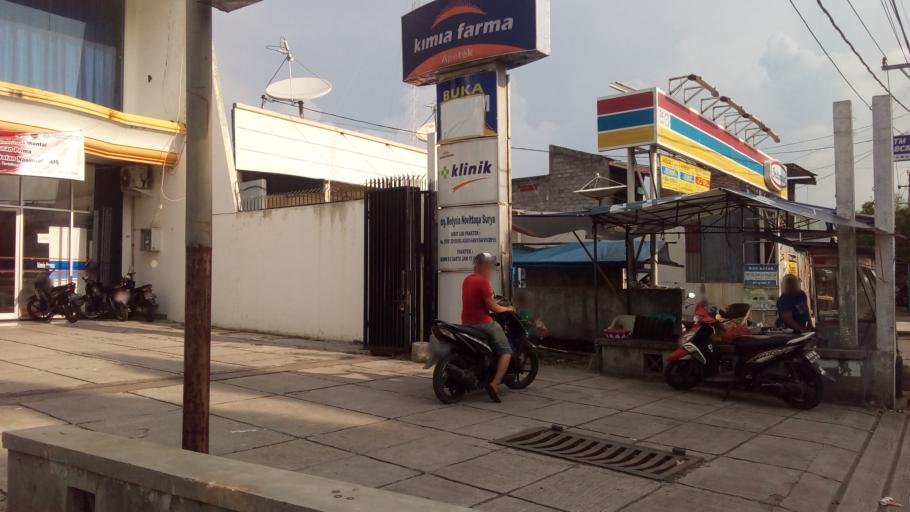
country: ID
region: Central Java
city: Semarang
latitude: -6.9853
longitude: 110.4483
